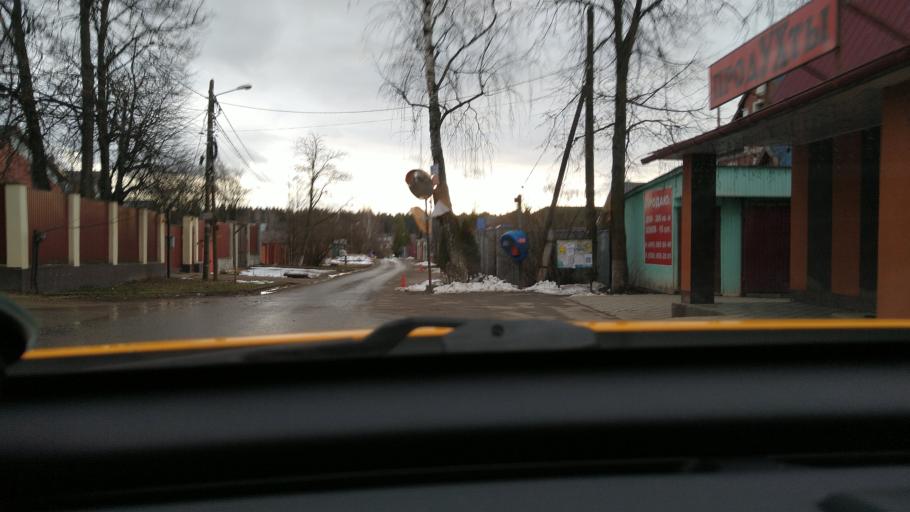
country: RU
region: Moskovskaya
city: Petrovo-Dal'neye
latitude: 55.7708
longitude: 37.1972
